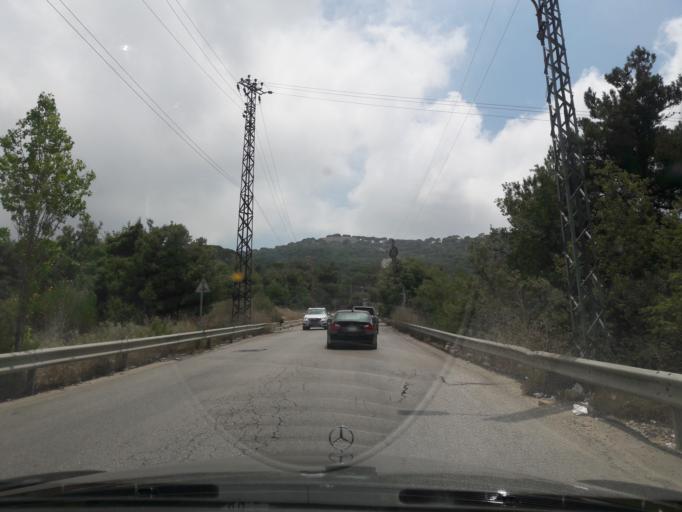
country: LB
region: Mont-Liban
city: Djounie
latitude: 33.9159
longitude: 35.6861
